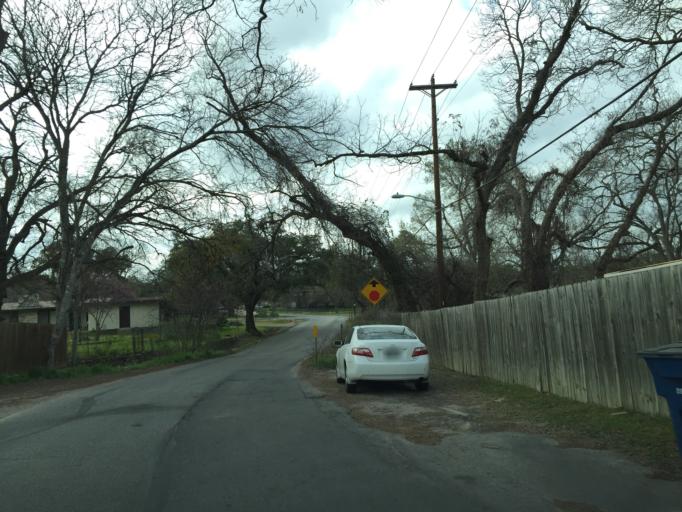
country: US
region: Texas
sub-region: Travis County
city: Wells Branch
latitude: 30.3821
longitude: -97.6769
